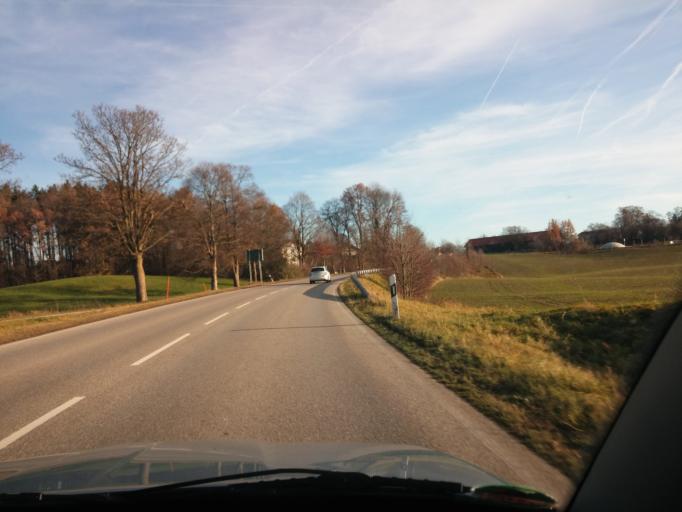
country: DE
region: Bavaria
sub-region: Upper Bavaria
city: Schnaitsee
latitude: 48.0306
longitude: 12.3651
